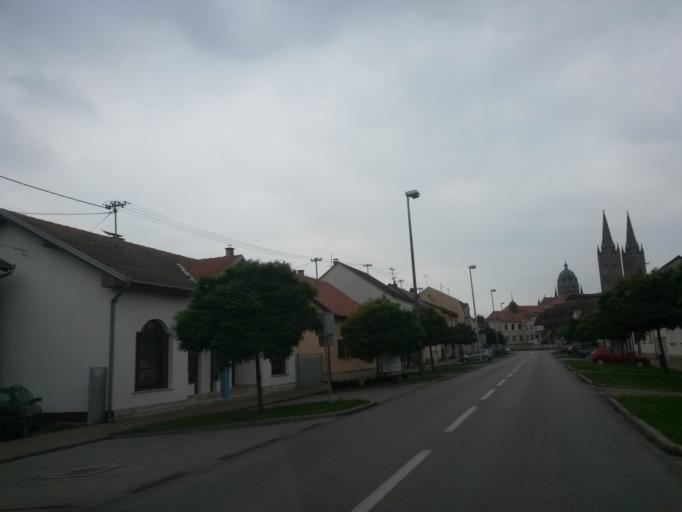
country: HR
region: Osjecko-Baranjska
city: Piskorevci
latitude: 45.3056
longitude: 18.4153
